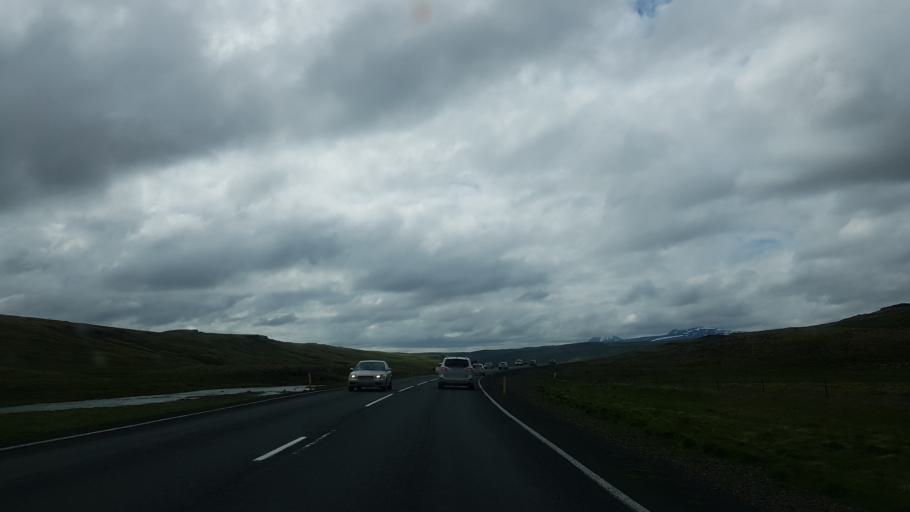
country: IS
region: West
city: Borgarnes
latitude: 64.9188
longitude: -21.1278
